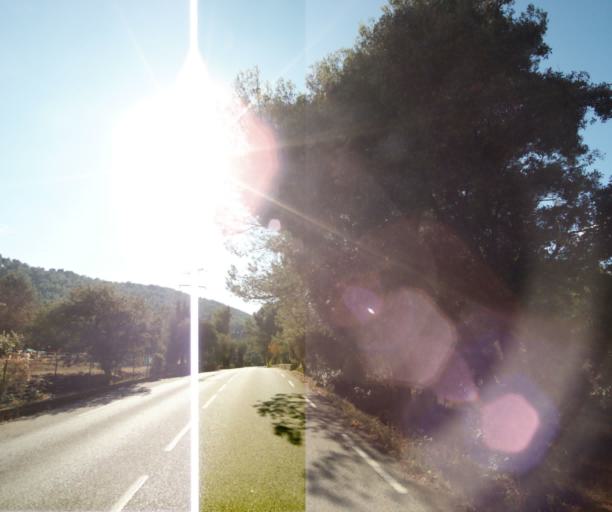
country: FR
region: Provence-Alpes-Cote d'Azur
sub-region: Departement des Bouches-du-Rhone
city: Ceyreste
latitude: 43.2247
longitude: 5.6498
